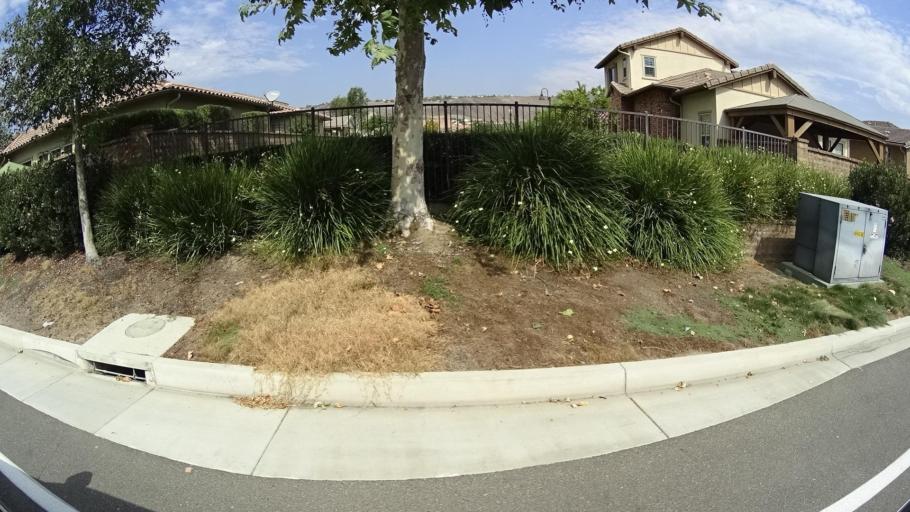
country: US
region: California
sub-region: Orange County
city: San Juan Capistrano
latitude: 33.5237
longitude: -117.6240
